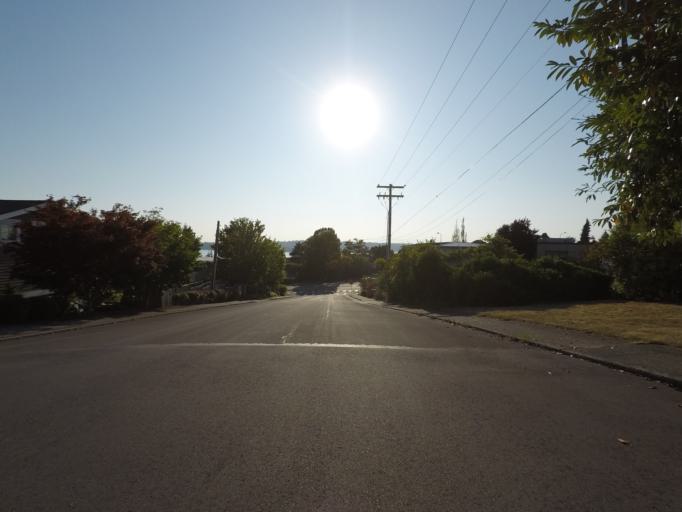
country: US
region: Washington
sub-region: King County
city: Kirkland
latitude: 47.6829
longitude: -122.2086
